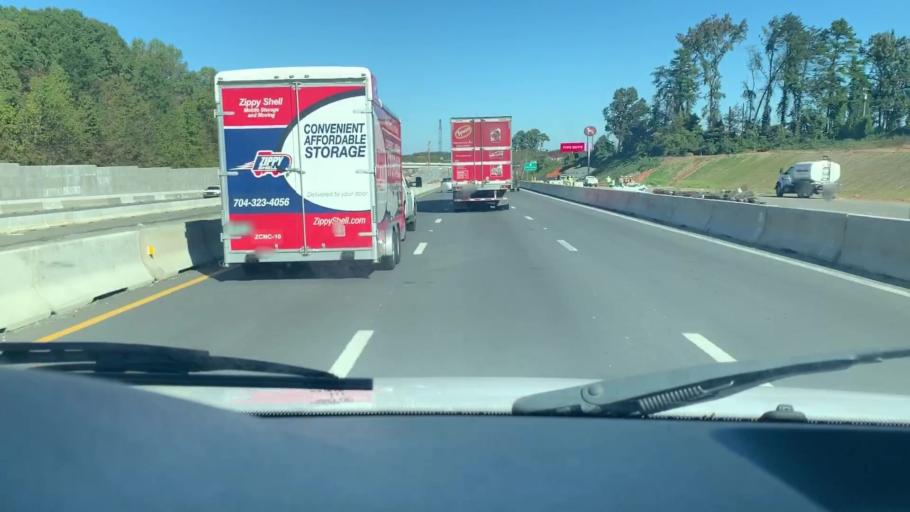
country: US
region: North Carolina
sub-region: Mecklenburg County
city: Huntersville
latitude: 35.3296
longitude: -80.8481
